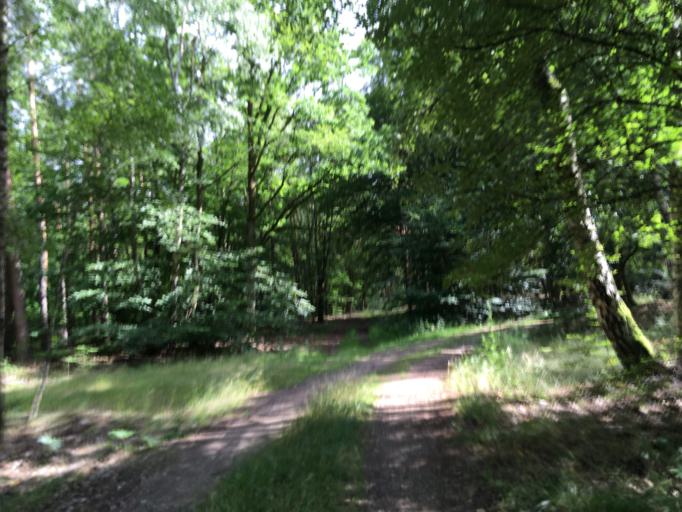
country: DE
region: Brandenburg
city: Bernau bei Berlin
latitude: 52.7256
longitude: 13.5484
